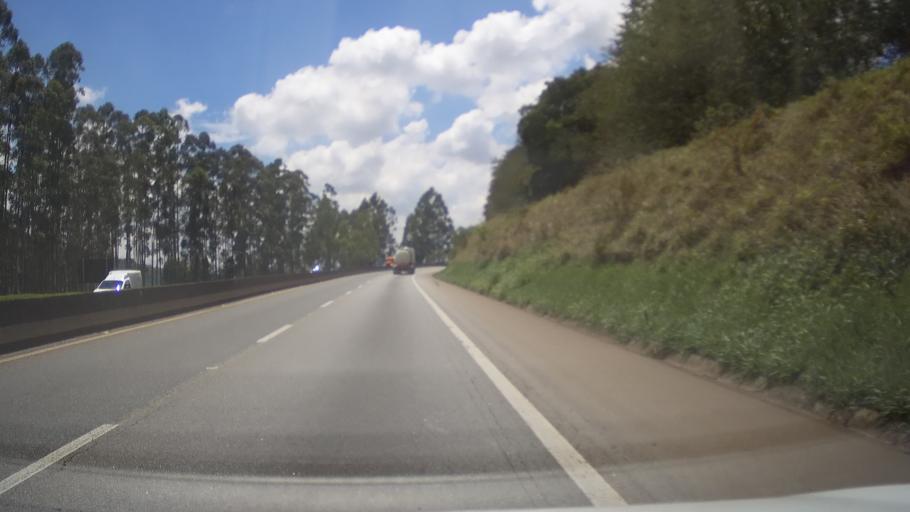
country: BR
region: Minas Gerais
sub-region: Campanha
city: Campanha
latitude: -21.8071
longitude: -45.4796
